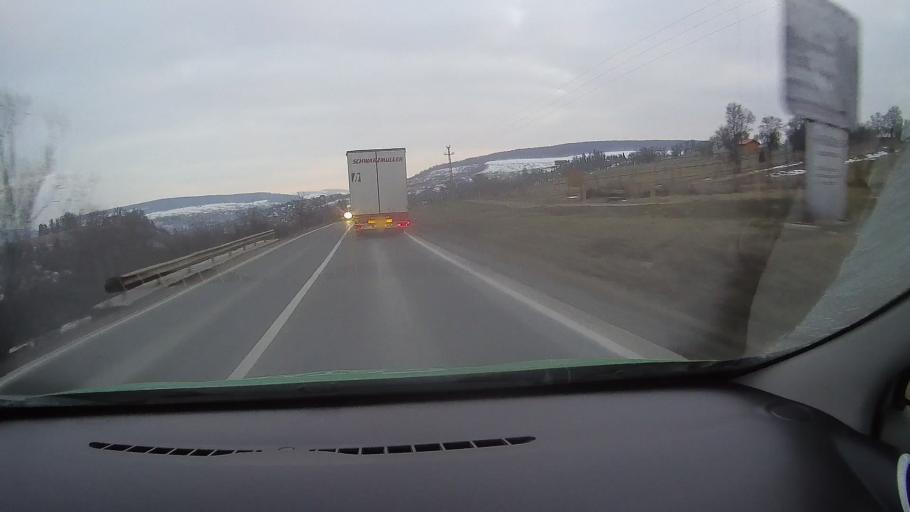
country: RO
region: Harghita
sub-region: Municipiul Odorheiu Secuiesc
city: Odorheiu Secuiesc
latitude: 46.3230
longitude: 25.2802
